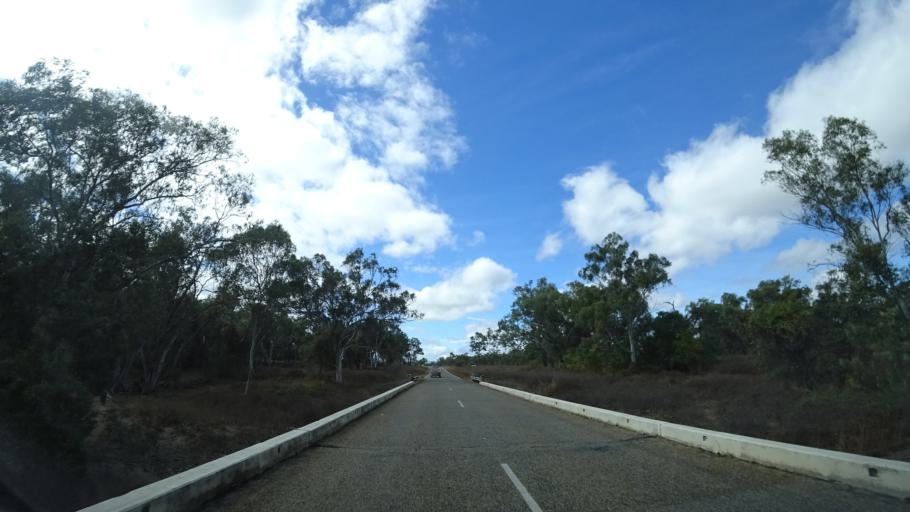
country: AU
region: Queensland
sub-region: Cairns
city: Port Douglas
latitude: -16.4969
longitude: 144.9764
